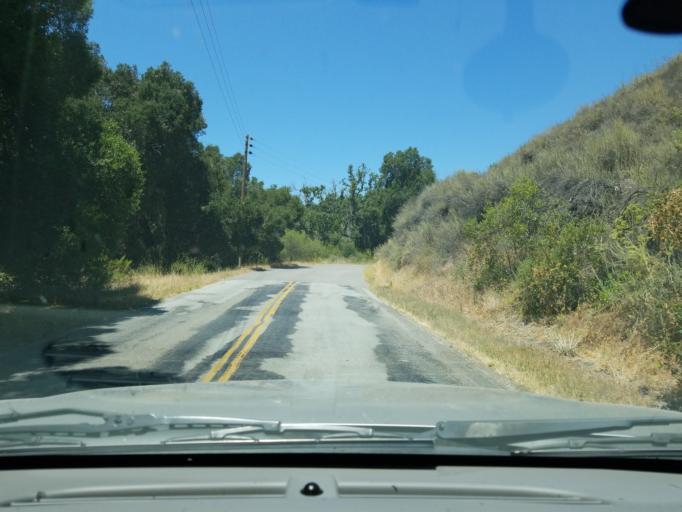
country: US
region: California
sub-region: Monterey County
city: Carmel Valley Village
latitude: 36.4332
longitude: -121.6278
